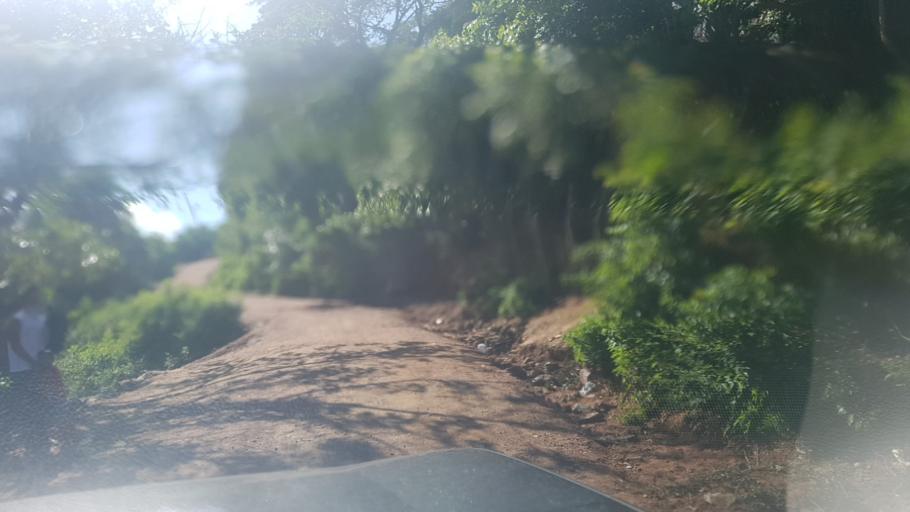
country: NI
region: Nueva Segovia
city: Ocotal
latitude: 13.6374
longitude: -86.6246
